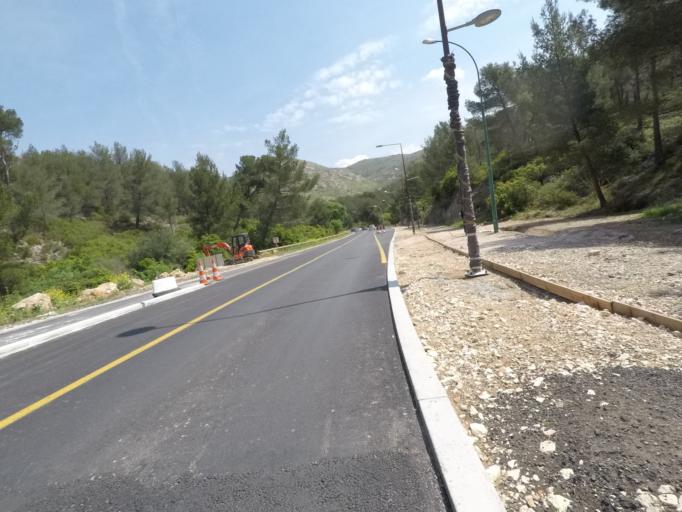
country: FR
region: Provence-Alpes-Cote d'Azur
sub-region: Departement des Bouches-du-Rhone
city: Marseille 09
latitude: 43.2391
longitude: 5.4365
